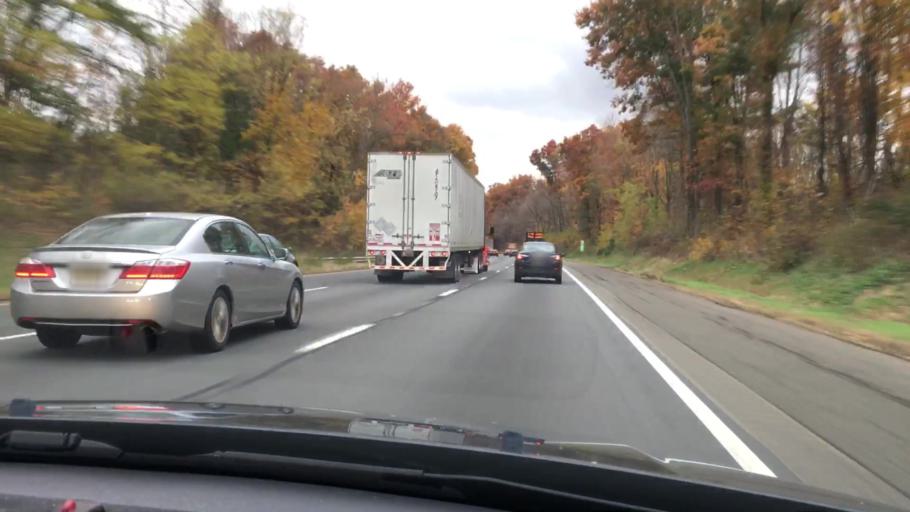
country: US
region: New Jersey
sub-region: Somerset County
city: Bernardsville
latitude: 40.7443
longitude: -74.5323
